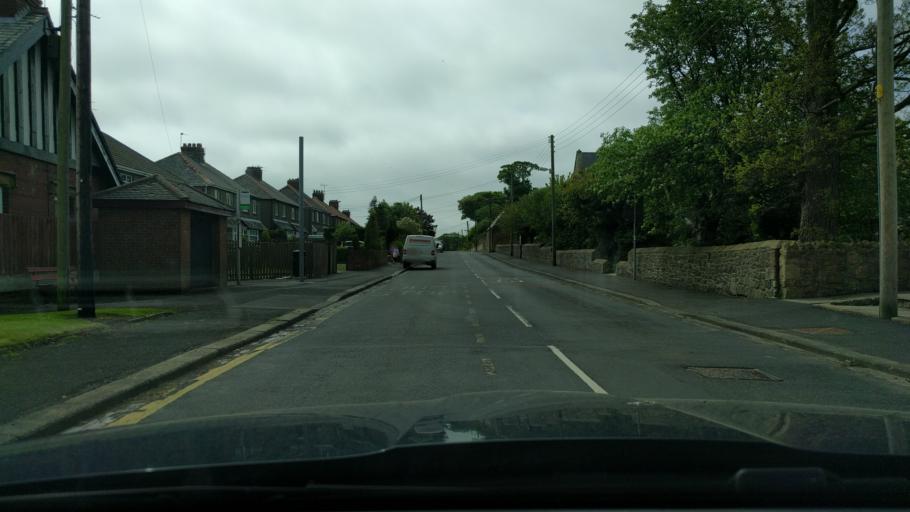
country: GB
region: England
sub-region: Northumberland
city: East Chevington
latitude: 55.2925
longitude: -1.6079
